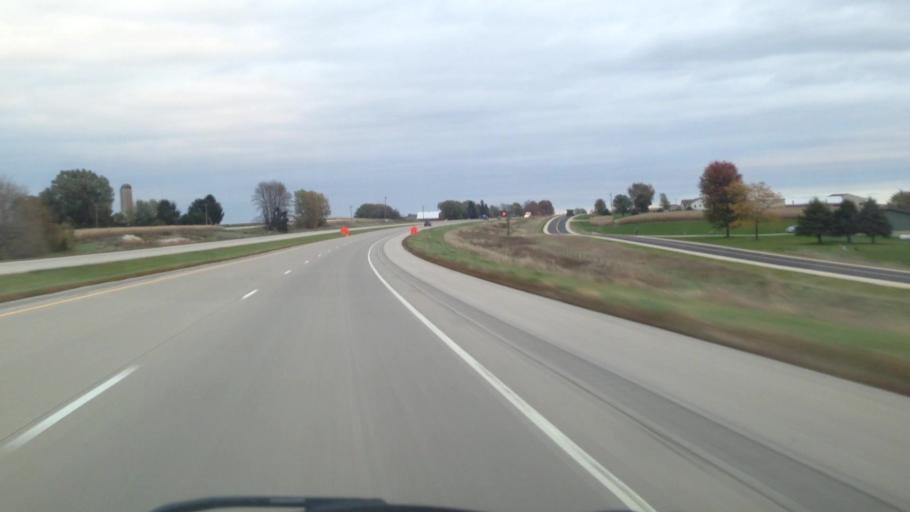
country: US
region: Wisconsin
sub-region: Trempealeau County
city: Trempealeau
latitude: 43.9254
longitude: -91.4832
